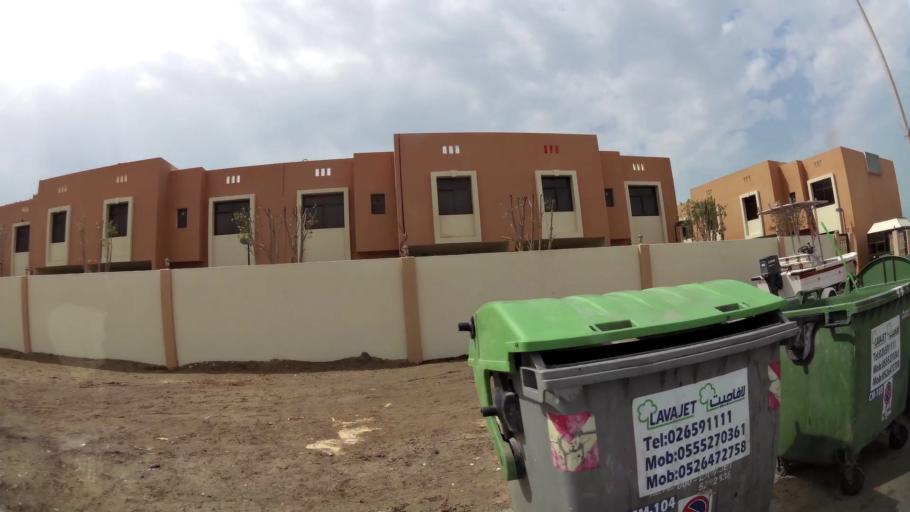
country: AE
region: Abu Dhabi
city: Abu Dhabi
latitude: 24.4381
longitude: 54.4505
